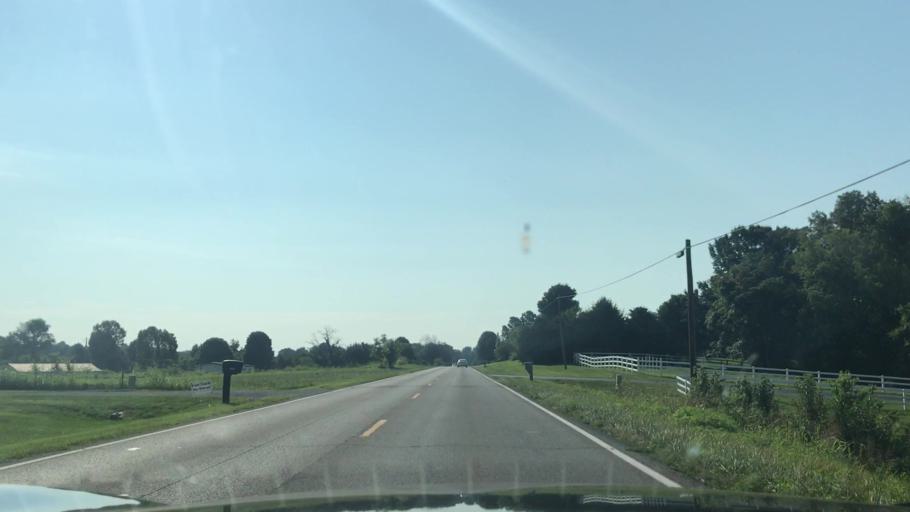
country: US
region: Kentucky
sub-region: Hart County
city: Horse Cave
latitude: 37.1700
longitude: -85.8526
